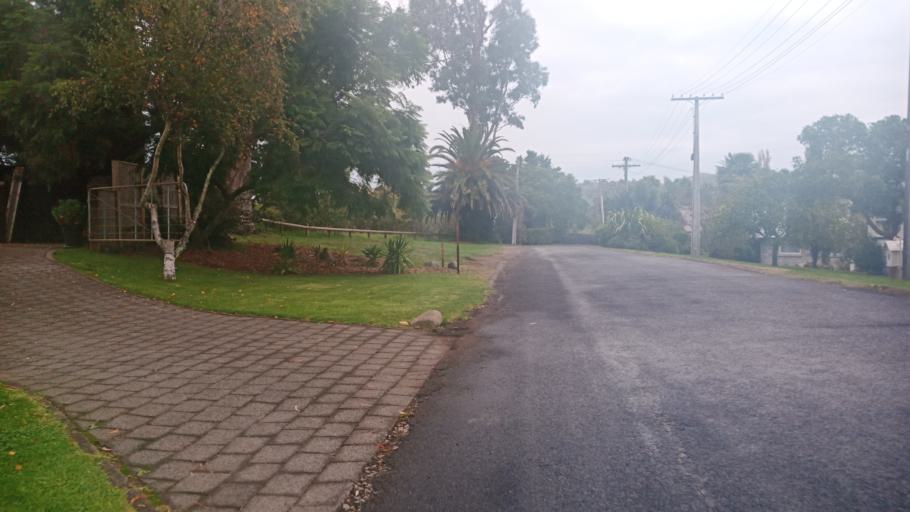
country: NZ
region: Gisborne
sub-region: Gisborne District
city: Gisborne
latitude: -38.6644
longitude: 178.0413
